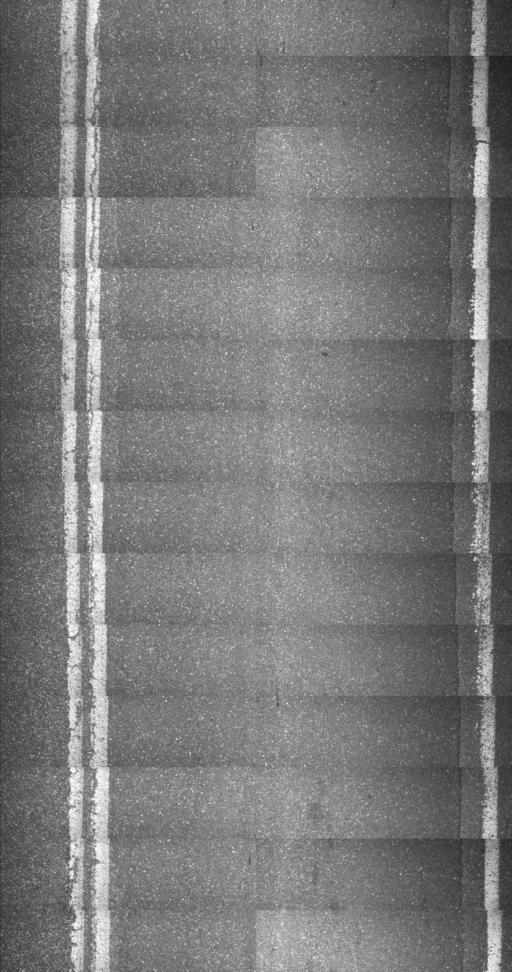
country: US
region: Vermont
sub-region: Orange County
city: Randolph
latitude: 43.9966
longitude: -72.6522
